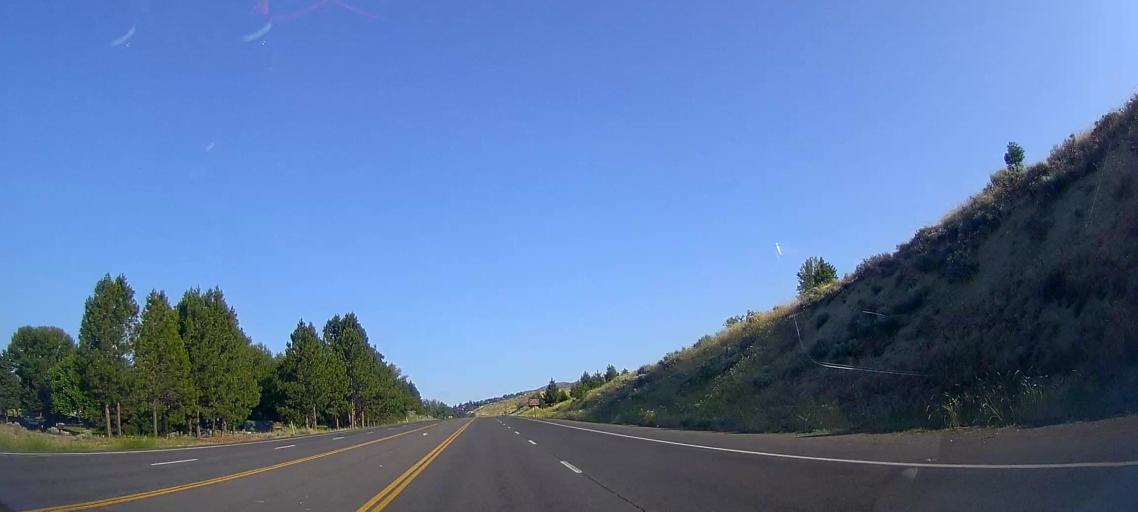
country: US
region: Oregon
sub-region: Klamath County
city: Altamont
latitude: 42.2183
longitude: -121.7484
